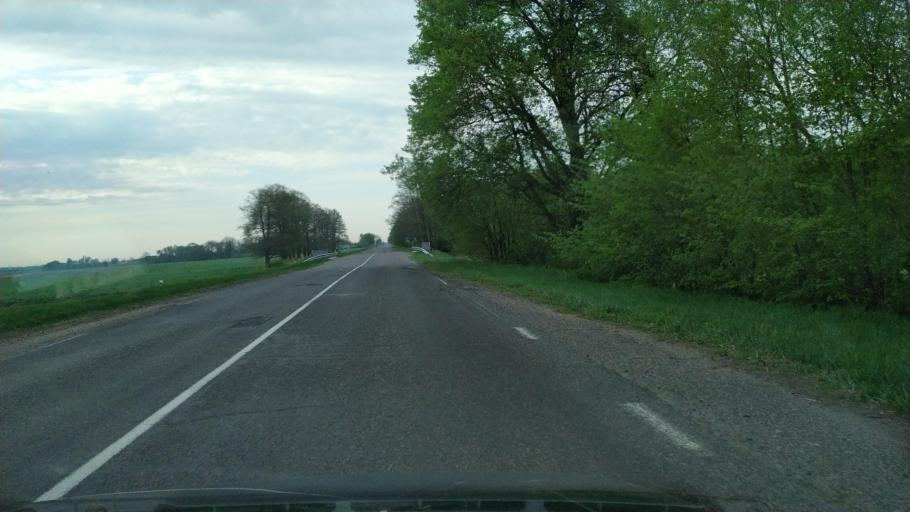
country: BY
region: Brest
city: Zhabinka
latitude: 52.2354
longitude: 23.9809
